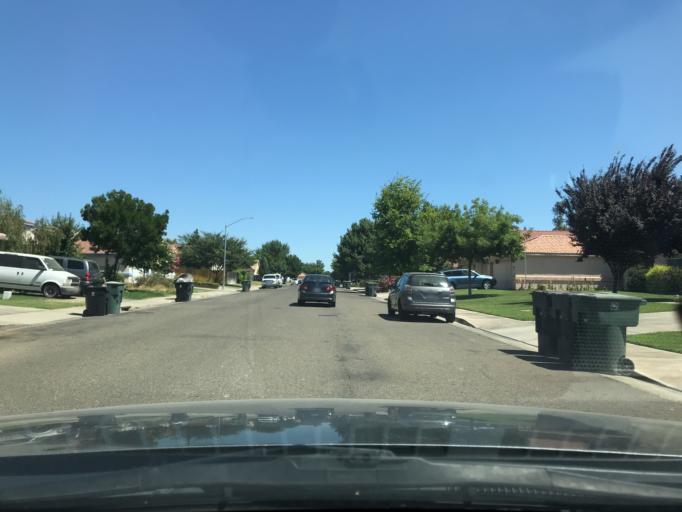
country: US
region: California
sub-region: Merced County
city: Atwater
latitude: 37.3434
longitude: -120.5859
